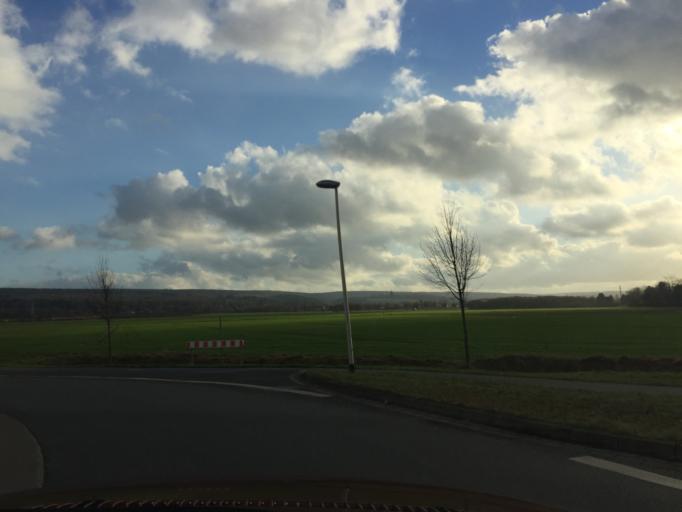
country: DE
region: Lower Saxony
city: Bevern
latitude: 51.8402
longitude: 9.4720
